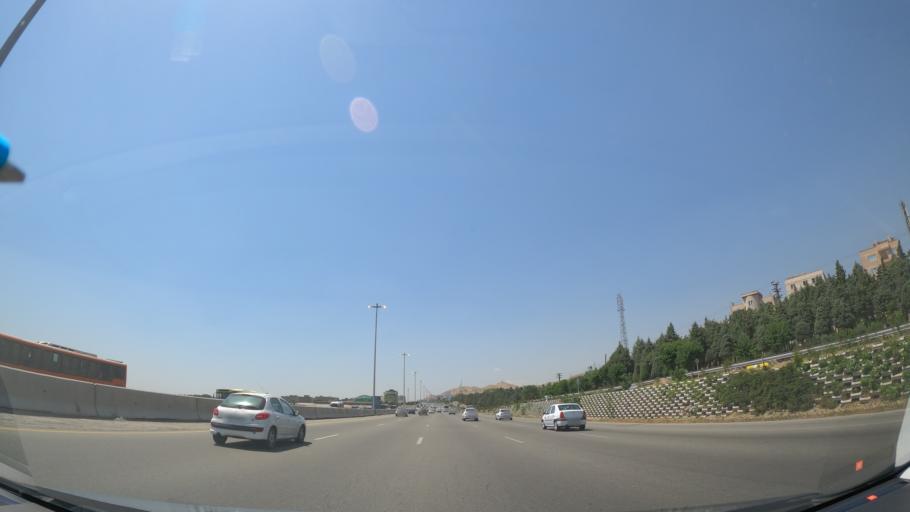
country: IR
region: Alborz
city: Karaj
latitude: 35.7758
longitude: 51.0387
